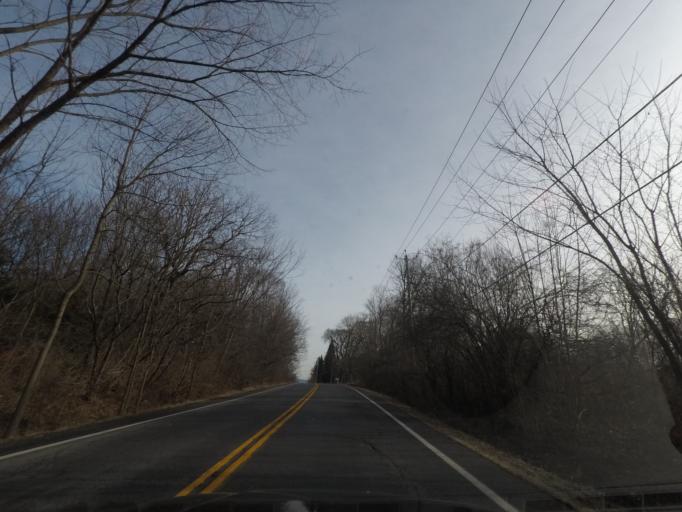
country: US
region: New York
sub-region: Saratoga County
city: Stillwater
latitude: 42.9851
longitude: -73.6785
